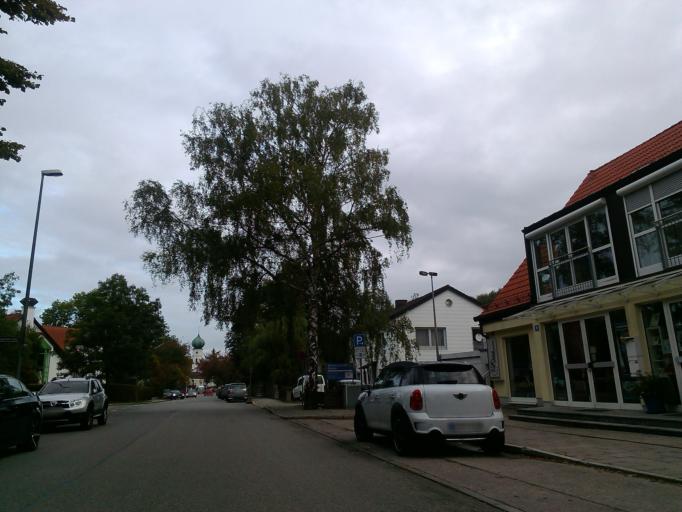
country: DE
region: Bavaria
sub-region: Upper Bavaria
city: Grobenzell
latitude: 48.1904
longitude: 11.3717
